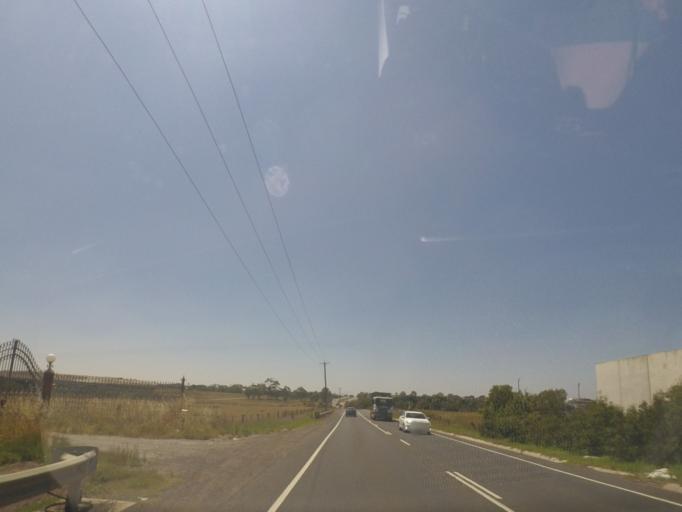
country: AU
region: Victoria
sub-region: Hume
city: Craigieburn
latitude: -37.5998
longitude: 144.9481
